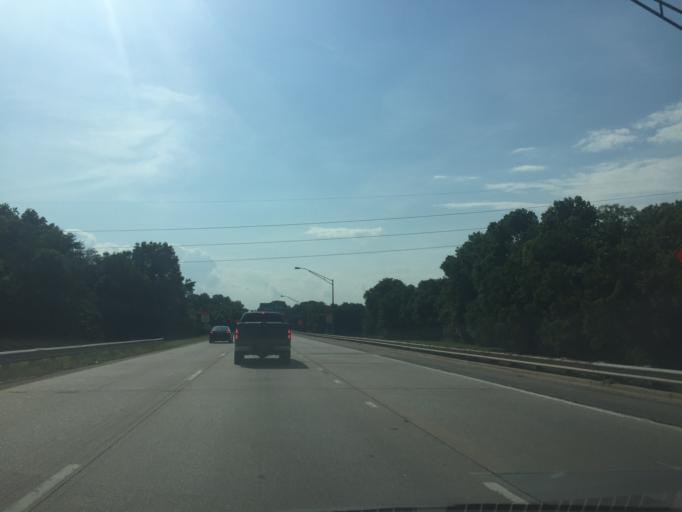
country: US
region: Georgia
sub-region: Chatham County
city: Savannah
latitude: 32.0706
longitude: -81.1297
